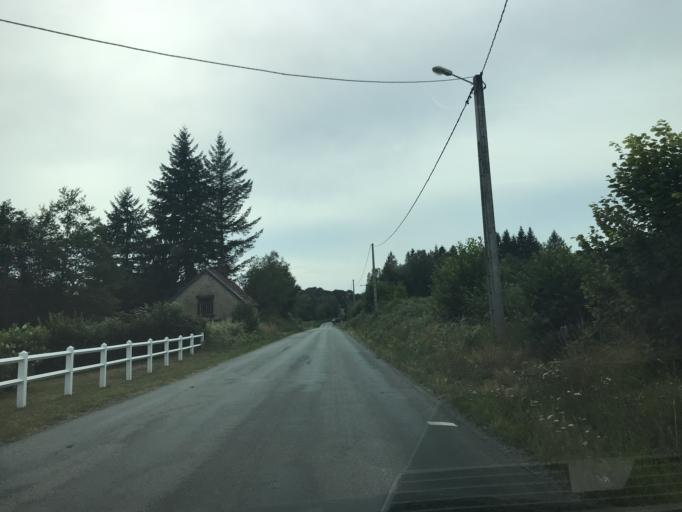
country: FR
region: Limousin
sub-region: Departement de la Correze
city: Neuvic
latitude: 45.3736
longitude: 2.2456
